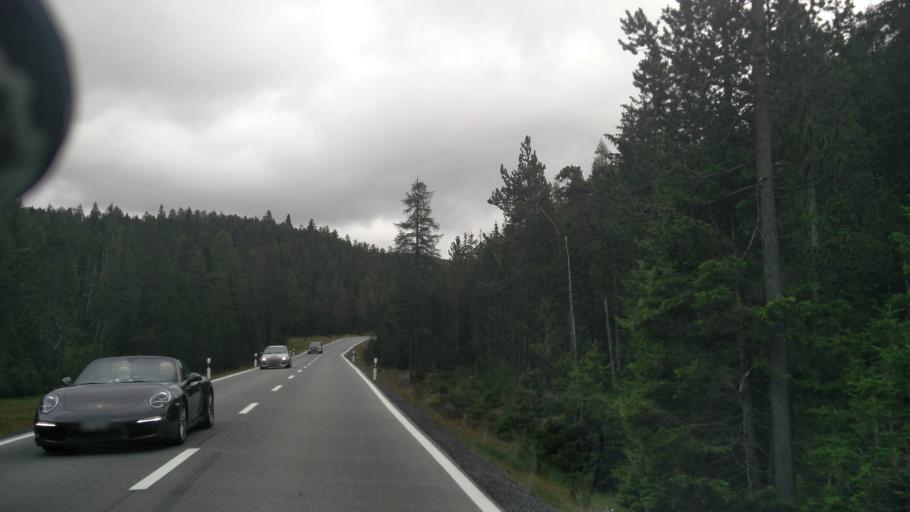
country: CH
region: Grisons
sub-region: Inn District
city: Zernez
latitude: 46.6826
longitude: 10.1549
